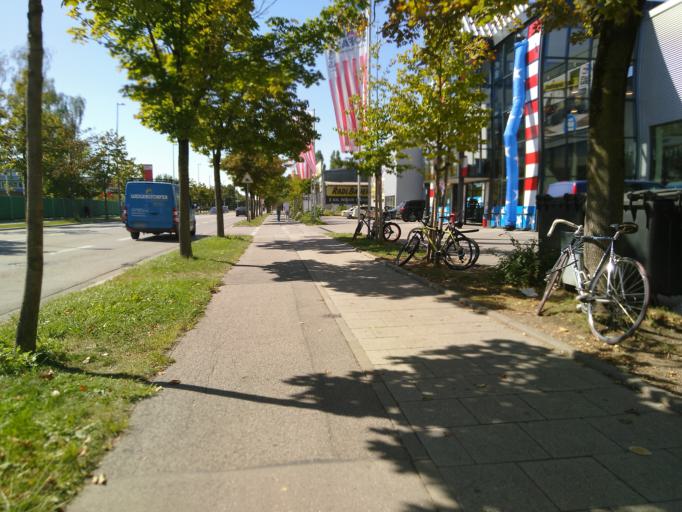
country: DE
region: Bavaria
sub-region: Upper Bavaria
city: Bogenhausen
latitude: 48.1928
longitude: 11.5930
